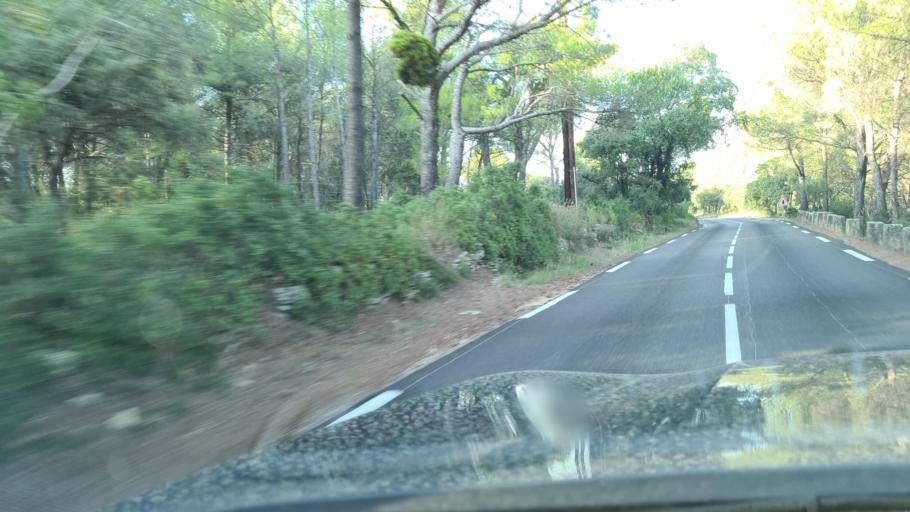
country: FR
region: Provence-Alpes-Cote d'Azur
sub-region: Departement des Bouches-du-Rhone
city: Cornillon-Confoux
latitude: 43.5702
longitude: 5.0745
